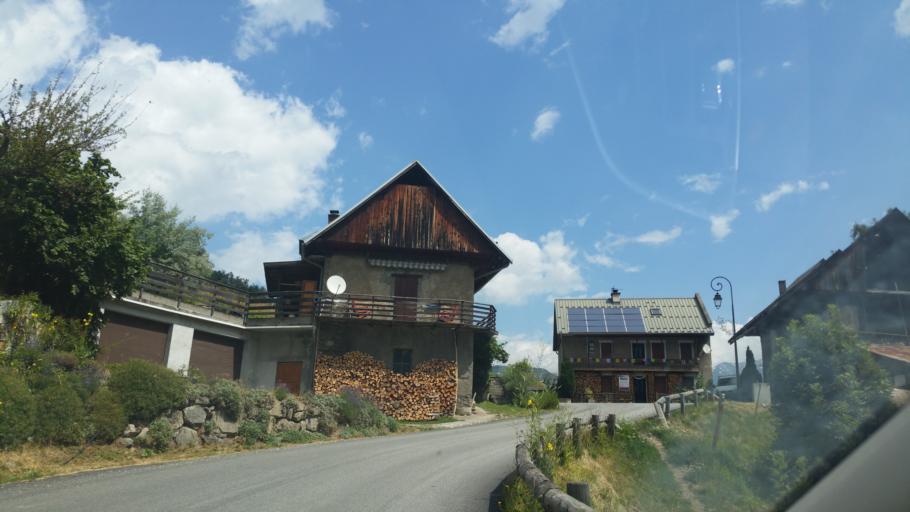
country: FR
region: Rhone-Alpes
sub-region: Departement de la Savoie
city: Saint-Jean-de-Maurienne
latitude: 45.2412
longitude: 6.3160
